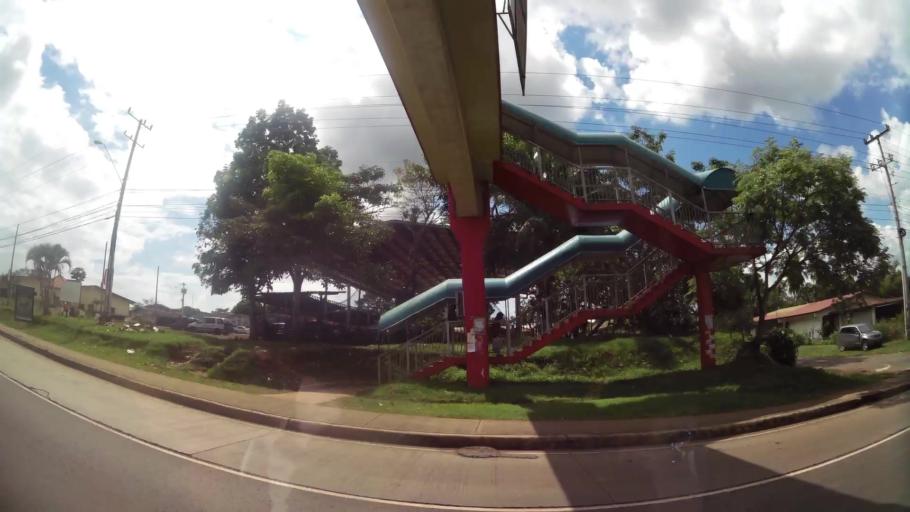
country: PA
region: Panama
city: Nuevo Arraijan
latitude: 8.9264
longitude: -79.7203
